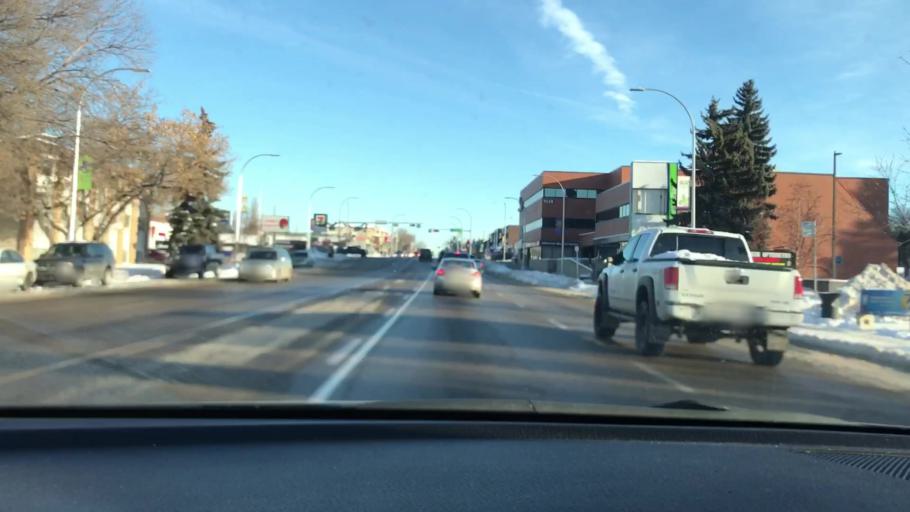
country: CA
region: Alberta
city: Edmonton
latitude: 53.5180
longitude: -113.4699
